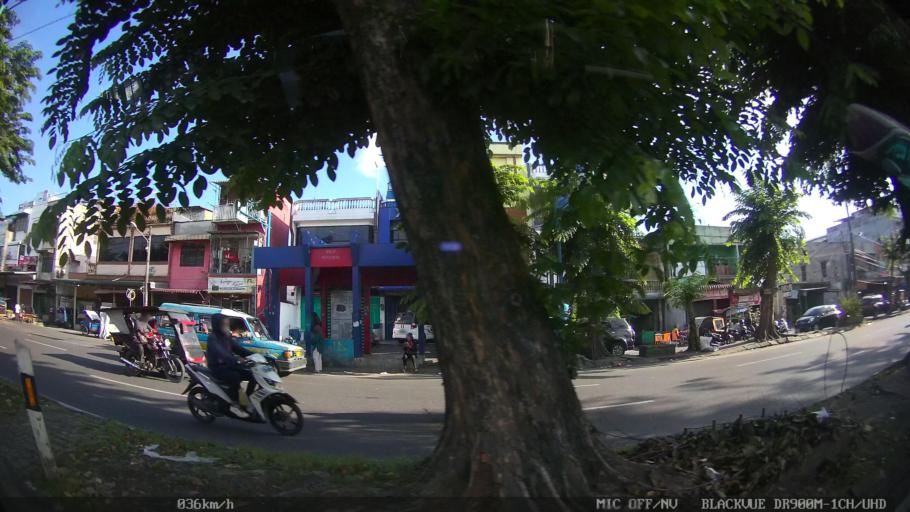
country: ID
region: North Sumatra
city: Medan
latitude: 3.5908
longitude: 98.6467
